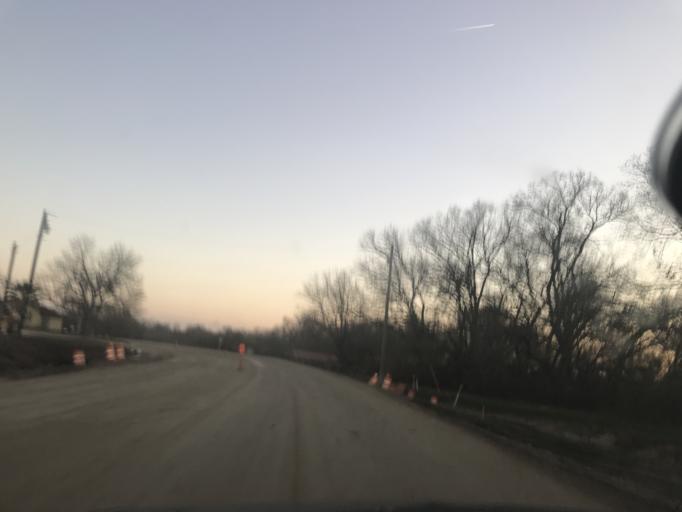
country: US
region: Texas
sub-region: Williamson County
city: Hutto
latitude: 30.5074
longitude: -97.5214
